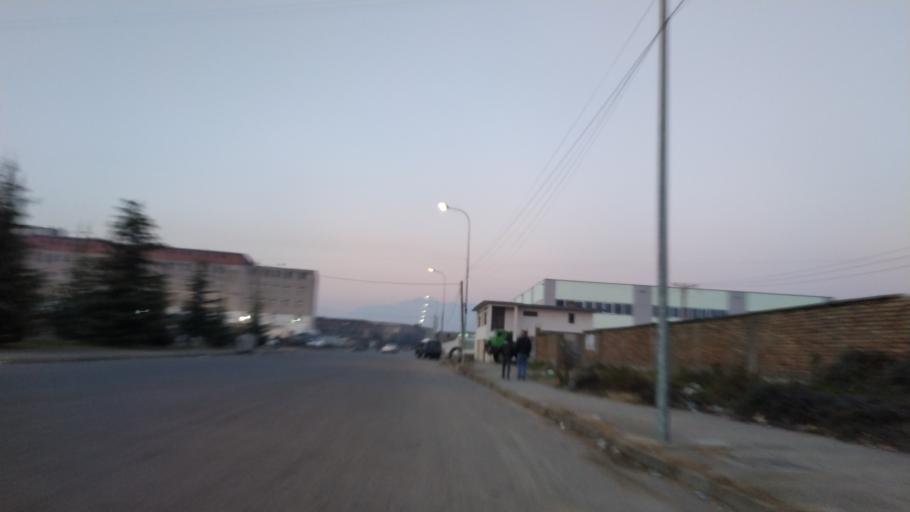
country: AL
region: Shkoder
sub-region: Rrethi i Shkodres
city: Shkoder
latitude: 42.0843
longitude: 19.5304
